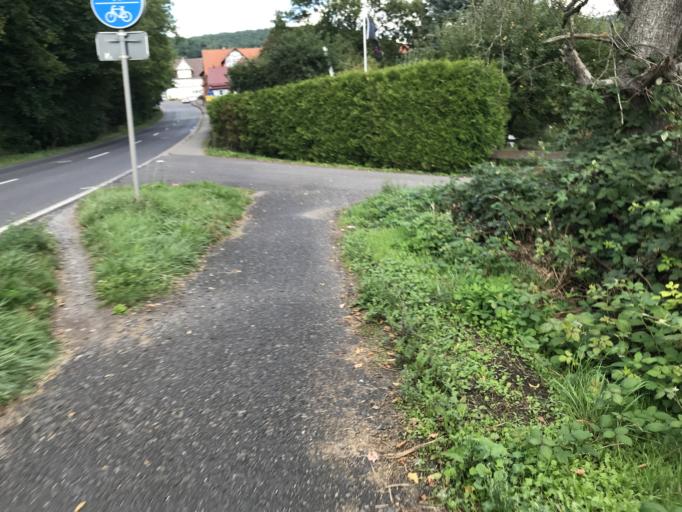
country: DE
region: Hesse
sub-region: Regierungsbezirk Kassel
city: Eschwege
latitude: 51.2119
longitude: 10.0153
